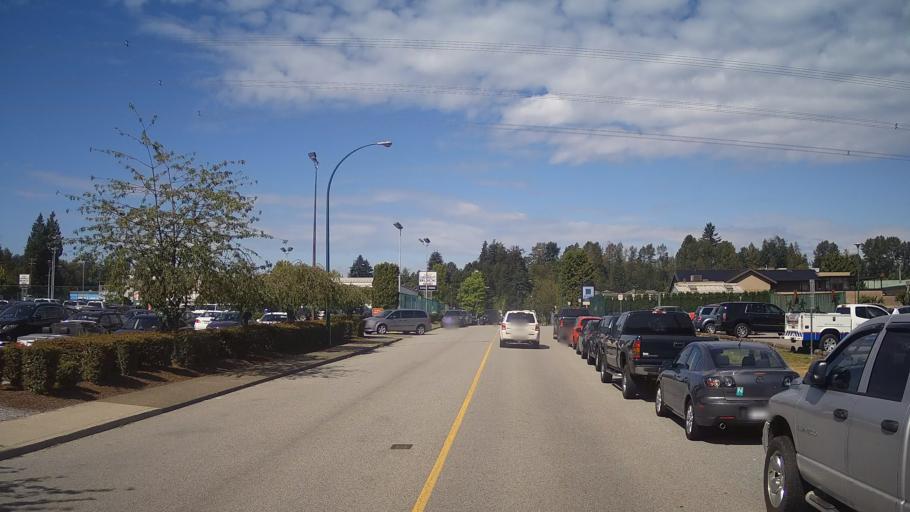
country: CA
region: British Columbia
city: Port Moody
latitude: 49.2789
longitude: -122.8146
